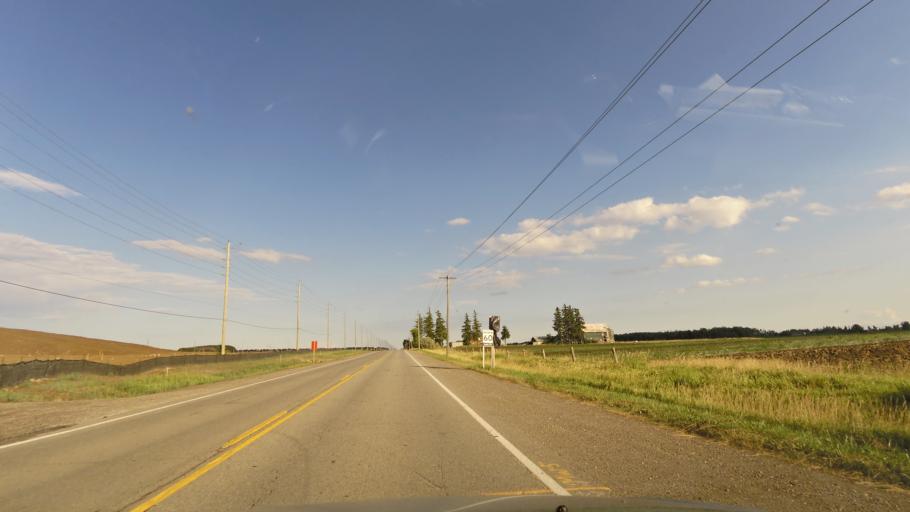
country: CA
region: Ontario
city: Brampton
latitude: 43.6907
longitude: -79.8620
